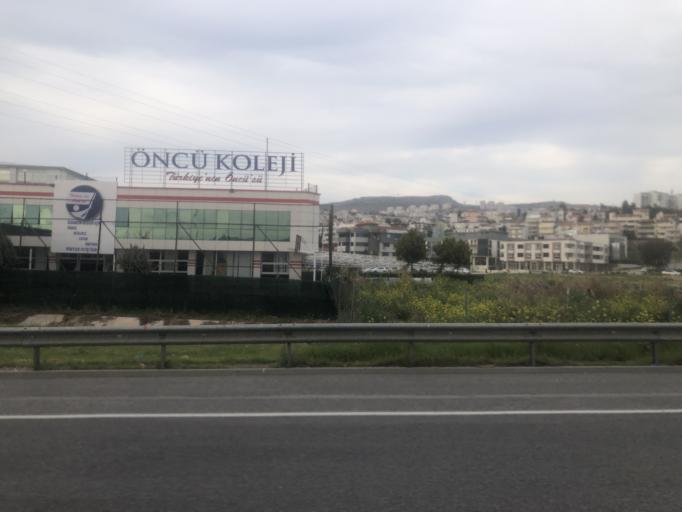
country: TR
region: Izmir
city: Karsiyaka
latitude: 38.4870
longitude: 27.0765
